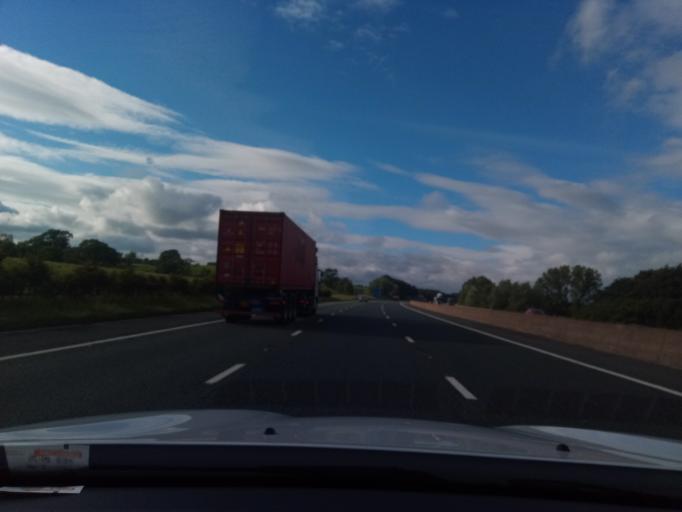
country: GB
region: England
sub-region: Cumbria
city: Penrith
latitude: 54.6858
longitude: -2.7901
